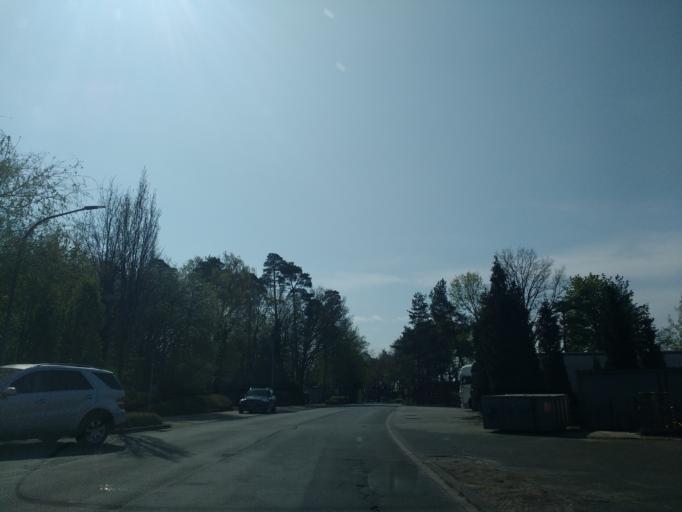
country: DE
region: North Rhine-Westphalia
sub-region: Regierungsbezirk Detmold
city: Hovelhof
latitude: 51.8301
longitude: 8.6533
